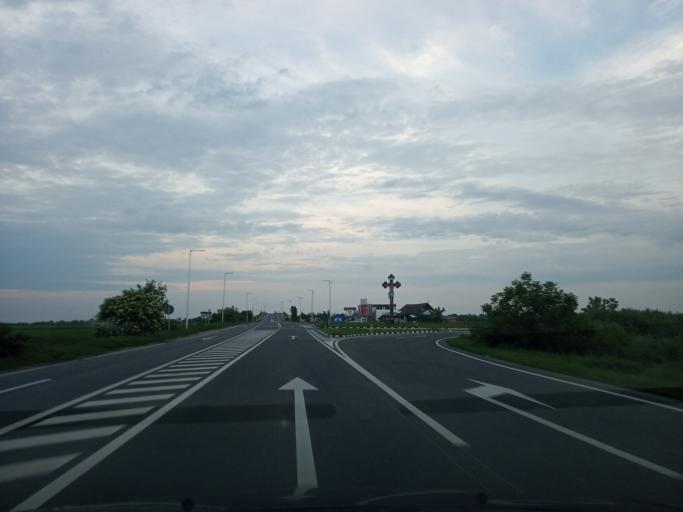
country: RO
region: Timis
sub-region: Comuna Voiteg
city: Voiteg
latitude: 45.4590
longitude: 21.2350
